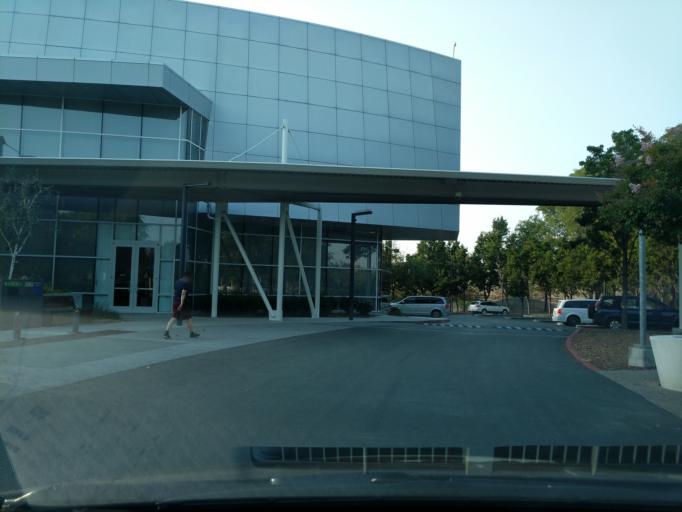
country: US
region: California
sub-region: Santa Clara County
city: Mountain View
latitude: 37.4221
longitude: -122.0829
